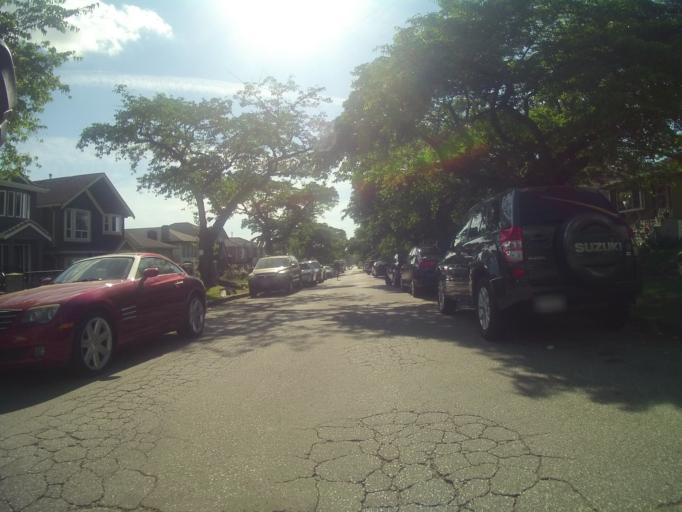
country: CA
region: British Columbia
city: Vancouver
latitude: 49.2165
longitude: -123.0883
